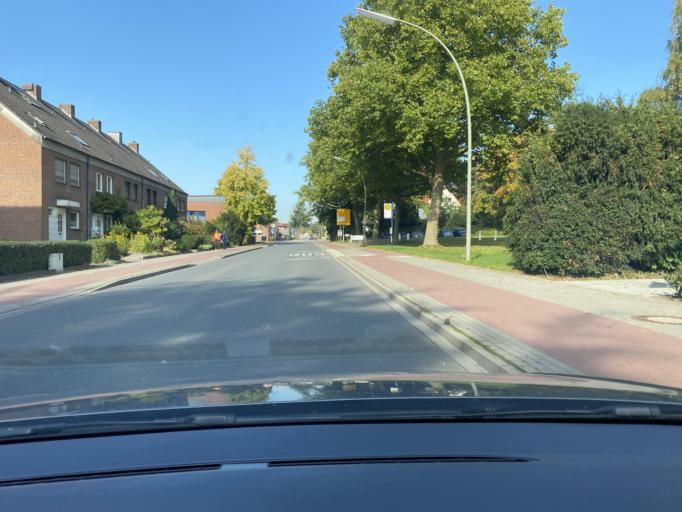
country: DE
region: North Rhine-Westphalia
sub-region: Regierungsbezirk Munster
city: Billerbeck
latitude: 51.9808
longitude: 7.2945
